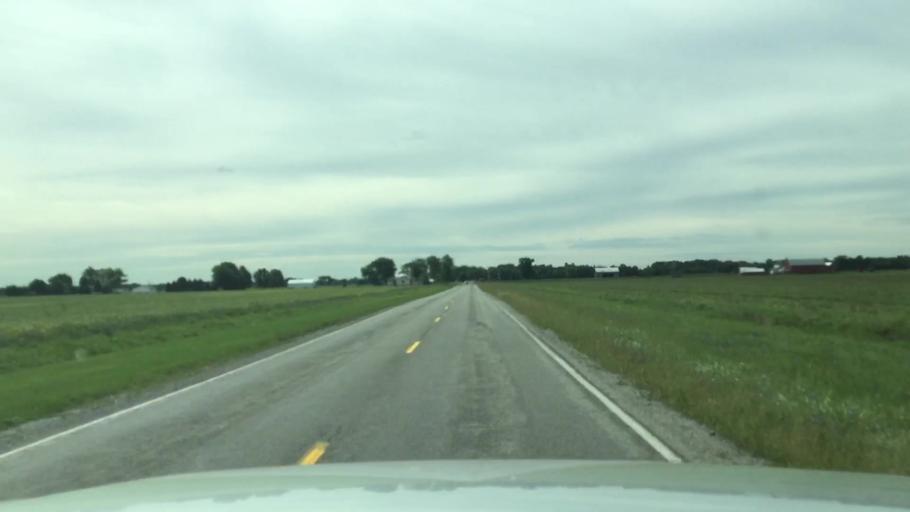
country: US
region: Michigan
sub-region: Genesee County
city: Montrose
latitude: 43.1377
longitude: -83.9882
